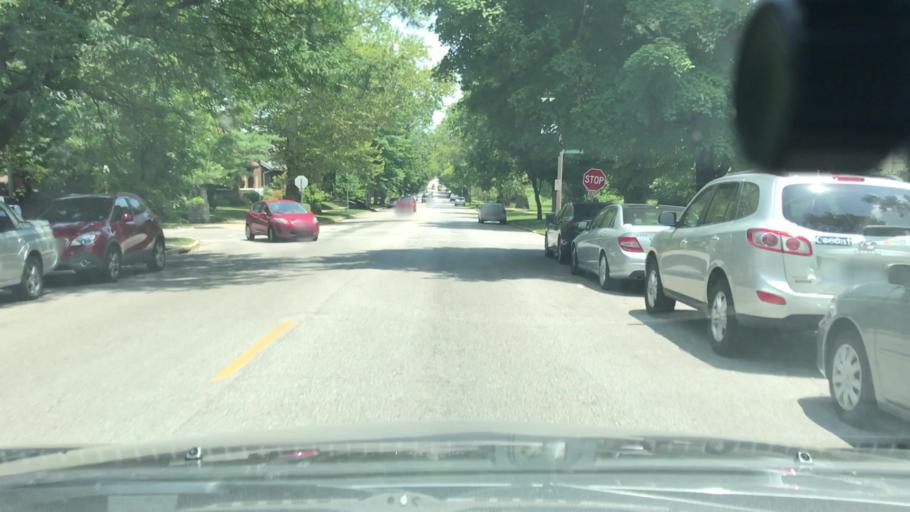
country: US
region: Missouri
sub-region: City of Saint Louis
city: St. Louis
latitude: 38.6082
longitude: -90.2523
